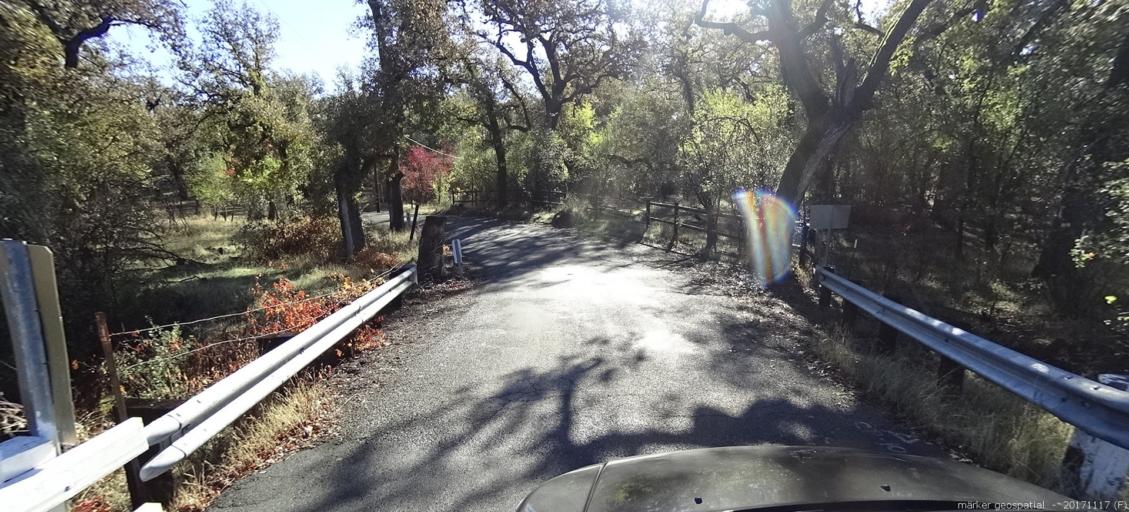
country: US
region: California
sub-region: Shasta County
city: Cottonwood
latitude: 40.4366
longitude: -122.1918
